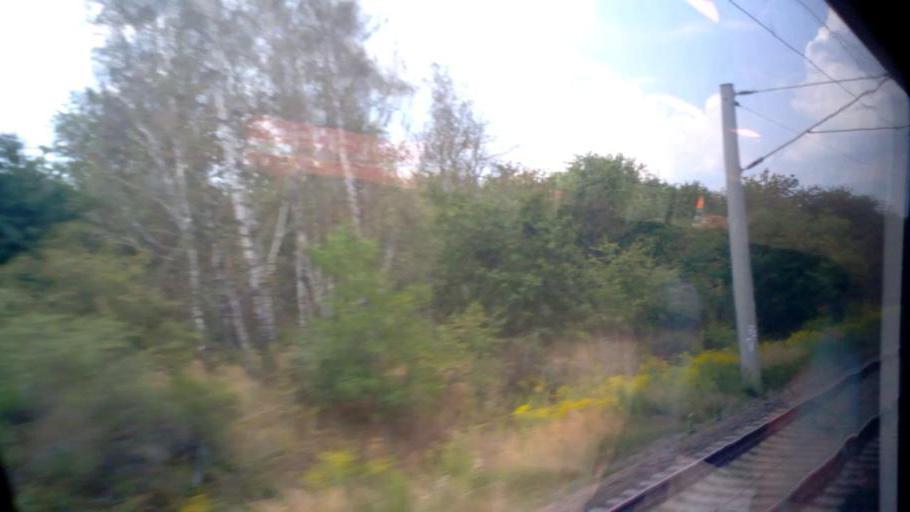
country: DE
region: Brandenburg
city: Grossbeeren
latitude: 52.3668
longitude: 13.2913
